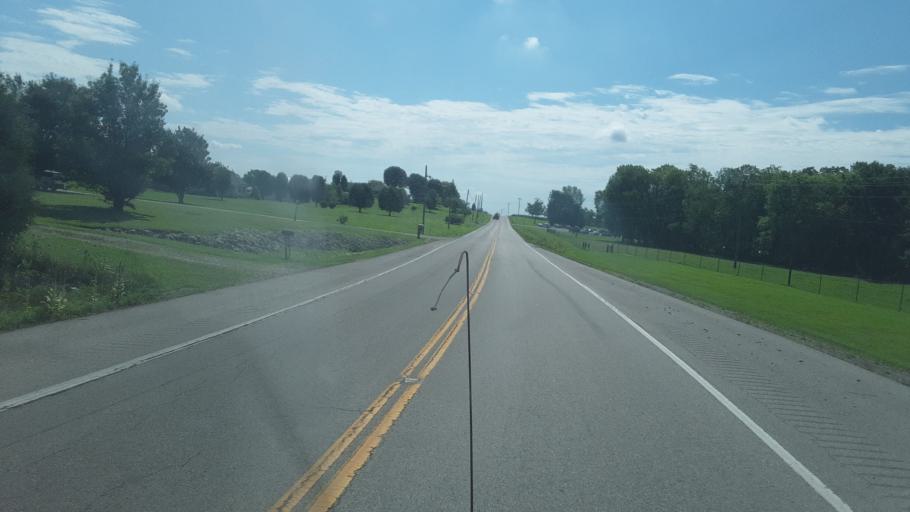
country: US
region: Kentucky
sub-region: Todd County
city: Elkton
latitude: 36.8207
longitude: -87.1986
